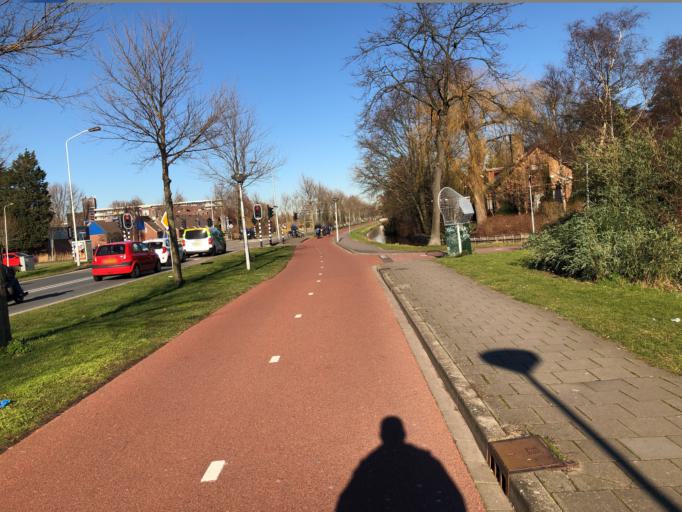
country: NL
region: North Holland
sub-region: Gemeente Uitgeest
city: Uitgeest
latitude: 52.4983
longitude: 4.7555
